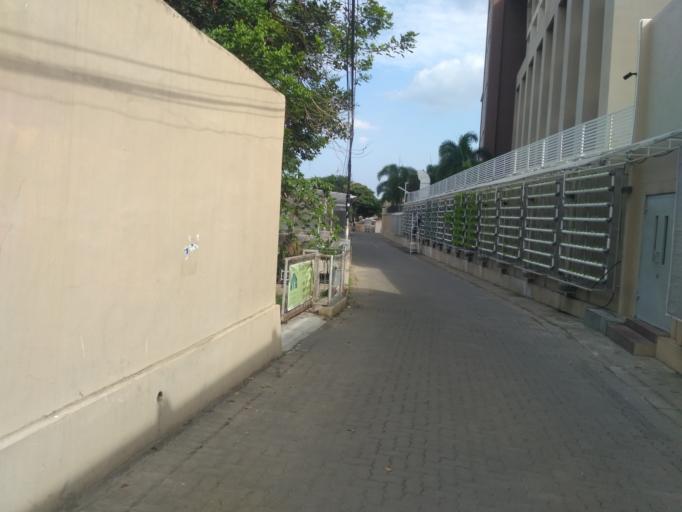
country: ID
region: Daerah Istimewa Yogyakarta
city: Depok
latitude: -7.7810
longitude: 110.4093
